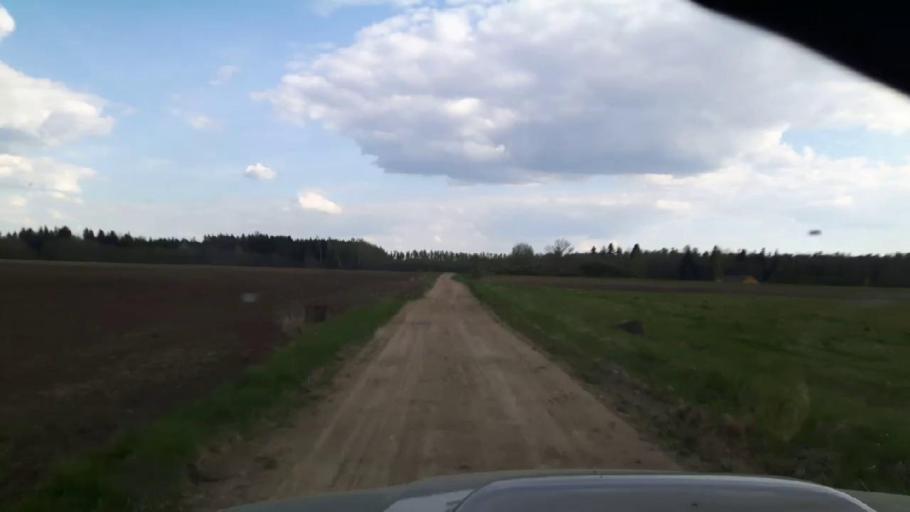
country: EE
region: Paernumaa
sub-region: Sindi linn
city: Sindi
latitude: 58.4348
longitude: 24.7691
